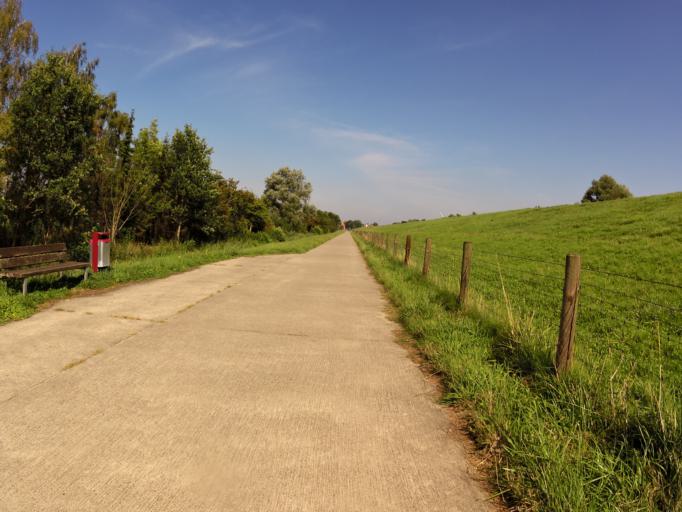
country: DE
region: Lower Saxony
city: Brake (Unterweser)
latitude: 53.2972
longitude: 8.4858
